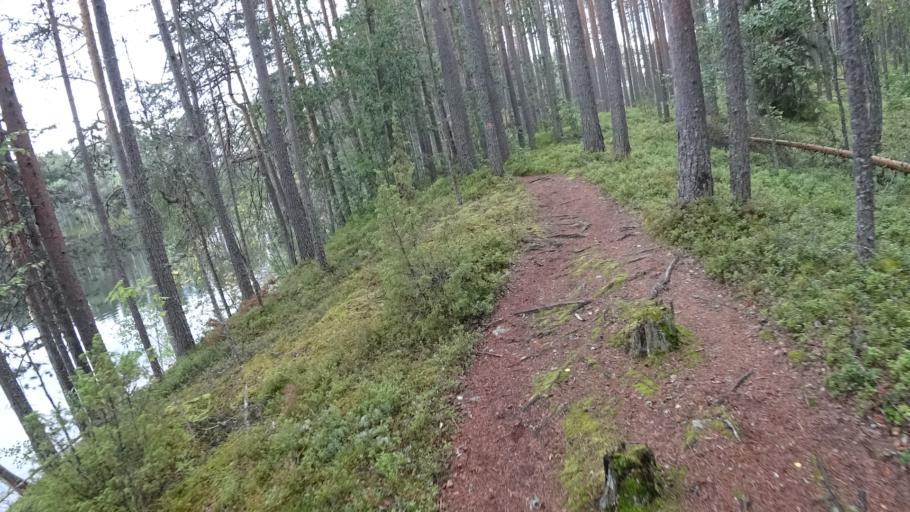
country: FI
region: North Karelia
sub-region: Joensuu
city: Ilomantsi
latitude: 62.5803
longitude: 31.1676
